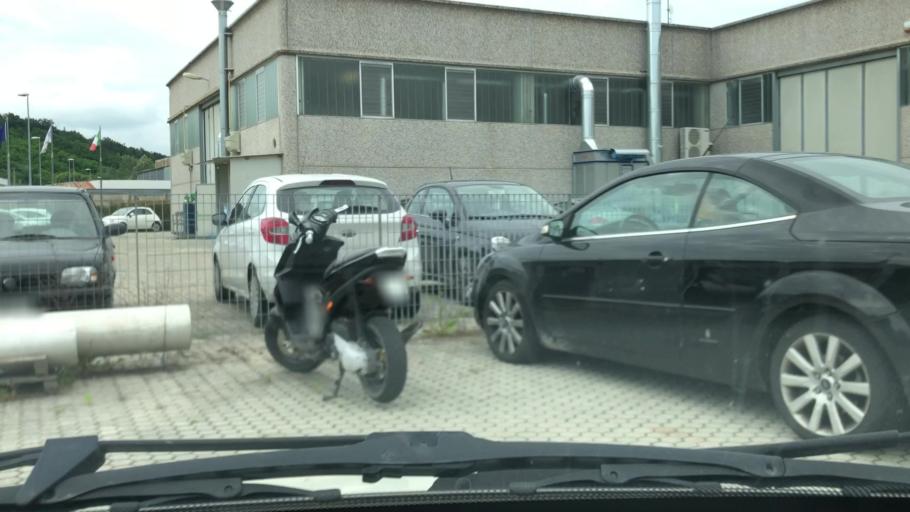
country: IT
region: Tuscany
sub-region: Province of Pisa
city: Calcinaia
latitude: 43.6909
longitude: 10.6259
